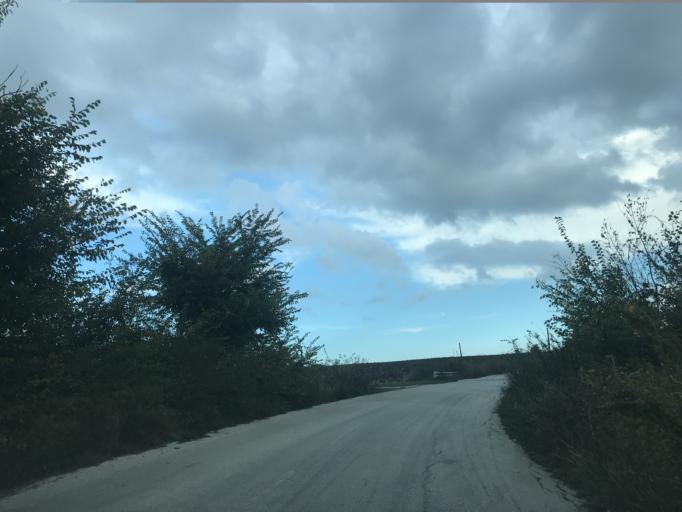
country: IT
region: Molise
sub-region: Provincia di Campobasso
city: Duronia
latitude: 41.6738
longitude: 14.4572
